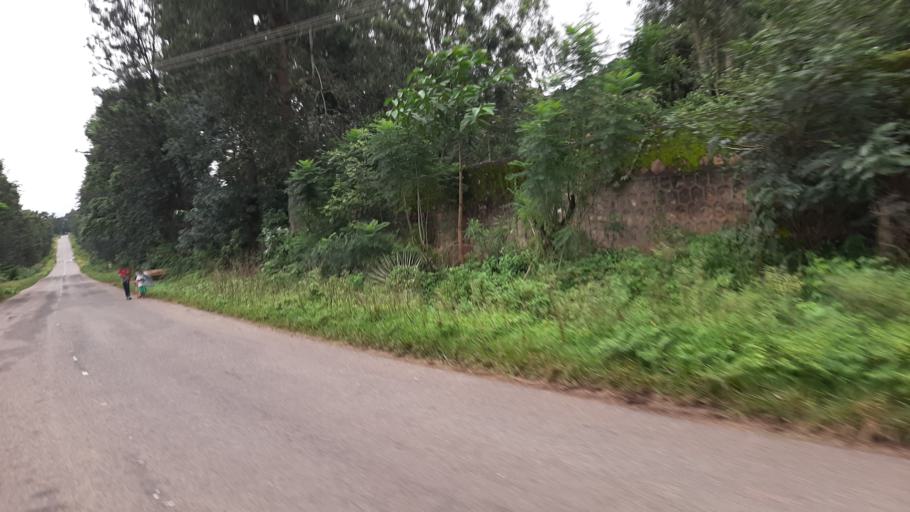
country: IN
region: Andhra Pradesh
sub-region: Vizianagaram District
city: Salur
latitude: 18.2928
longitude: 82.9192
